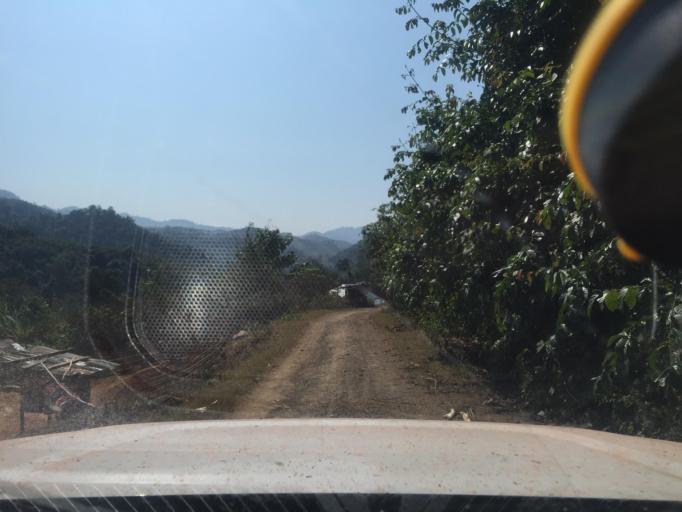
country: LA
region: Phongsali
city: Phongsali
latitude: 21.6582
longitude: 102.4219
